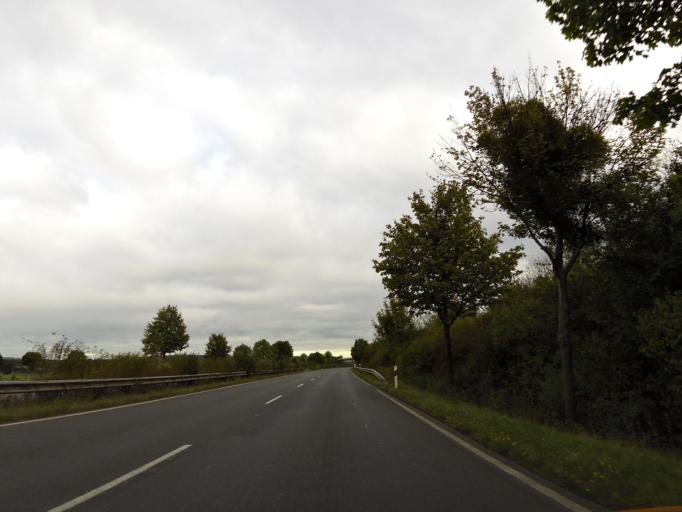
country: DE
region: Lower Saxony
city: Goettingen
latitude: 51.5613
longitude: 9.9202
